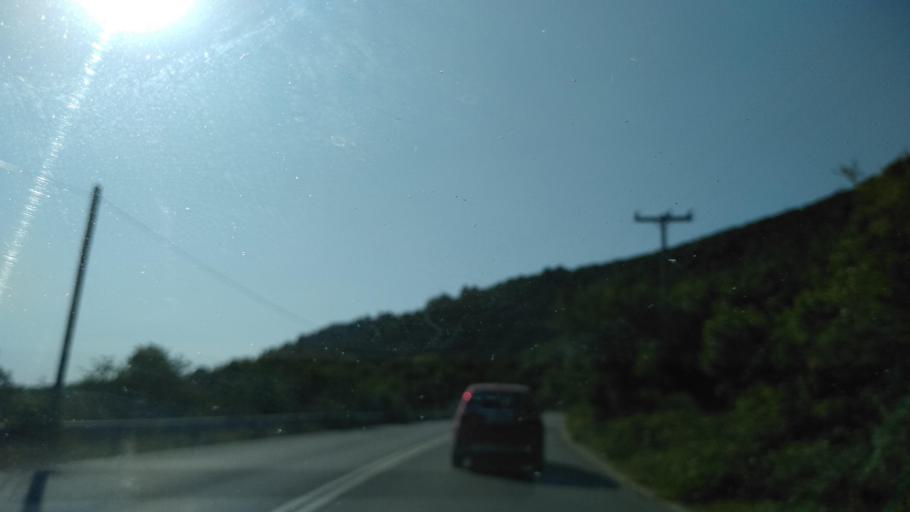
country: GR
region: Central Macedonia
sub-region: Nomos Chalkidikis
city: Stratonion
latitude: 40.5796
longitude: 23.8078
